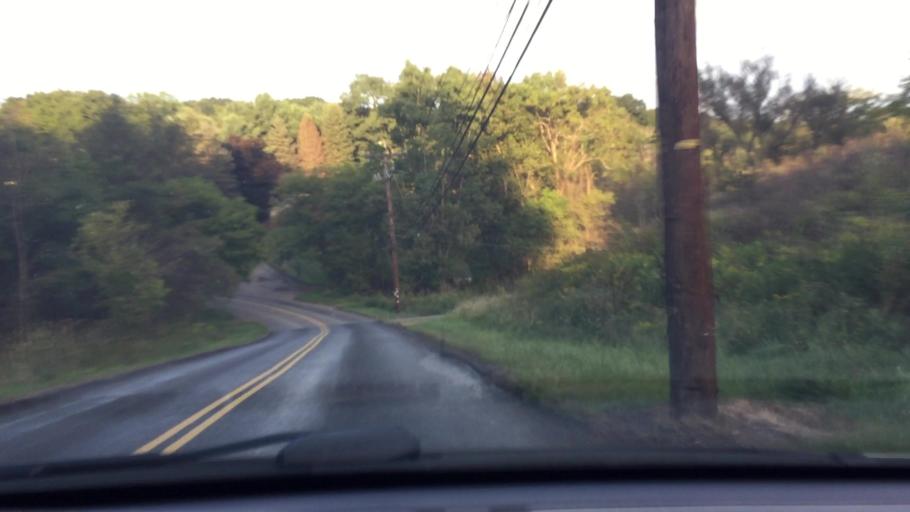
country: US
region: Pennsylvania
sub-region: Allegheny County
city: Plum
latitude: 40.4524
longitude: -79.7490
